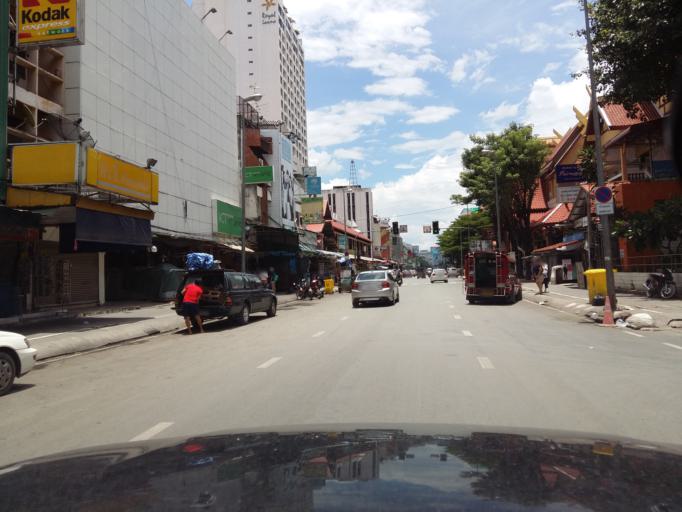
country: TH
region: Chiang Mai
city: Chiang Mai
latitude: 18.7857
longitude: 99.0007
